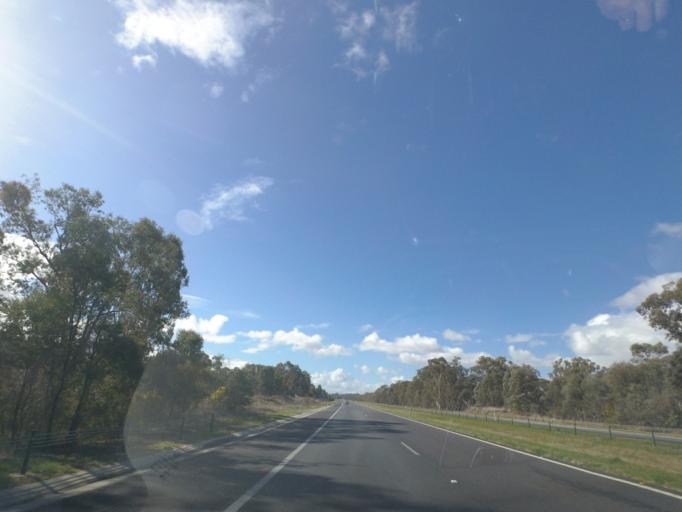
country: AU
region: New South Wales
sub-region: Albury Municipality
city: Lavington
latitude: -36.0485
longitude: 146.9642
